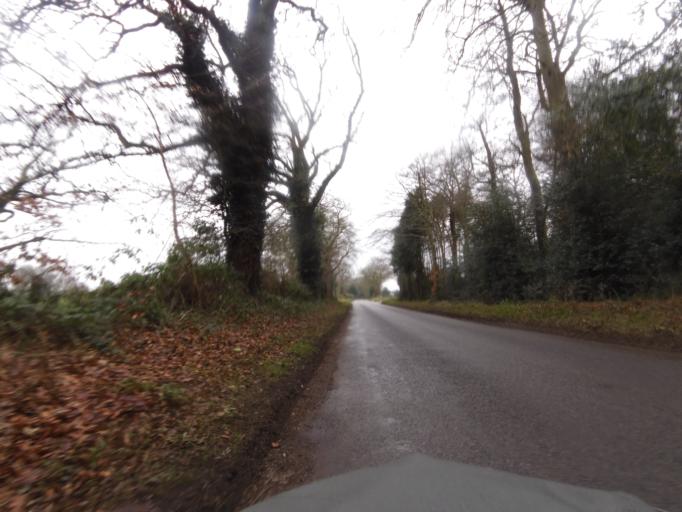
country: GB
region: England
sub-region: Norfolk
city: Briston
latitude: 52.8601
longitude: 1.0649
